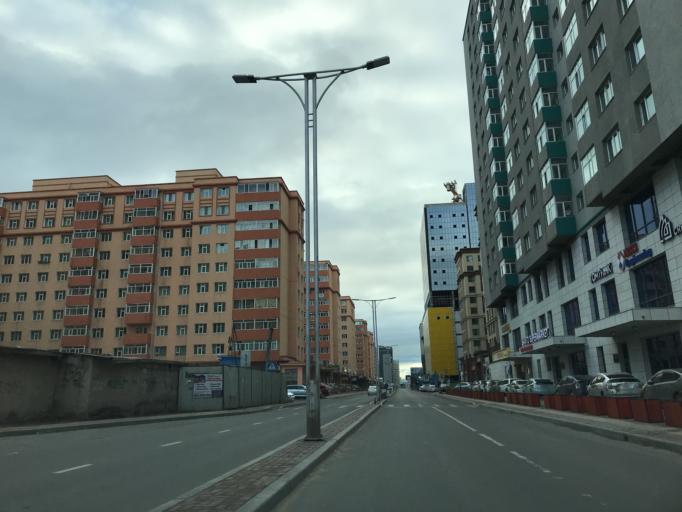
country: MN
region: Ulaanbaatar
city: Ulaanbaatar
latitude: 47.9044
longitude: 106.9311
